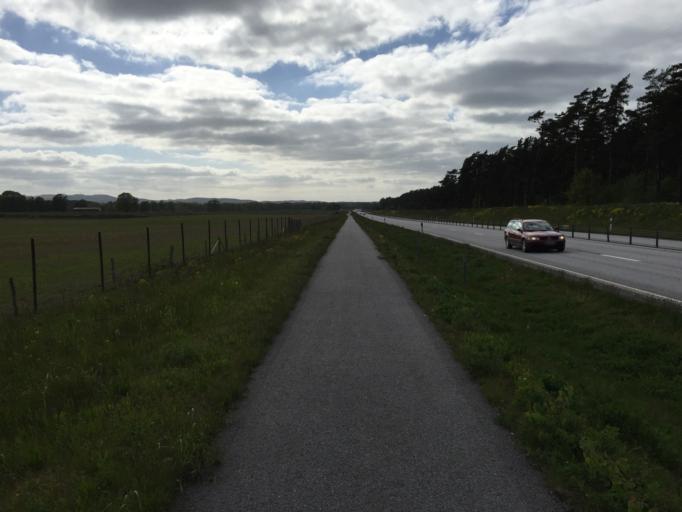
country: SE
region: Skane
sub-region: Sjobo Kommun
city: Blentarp
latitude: 55.6391
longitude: 13.5611
